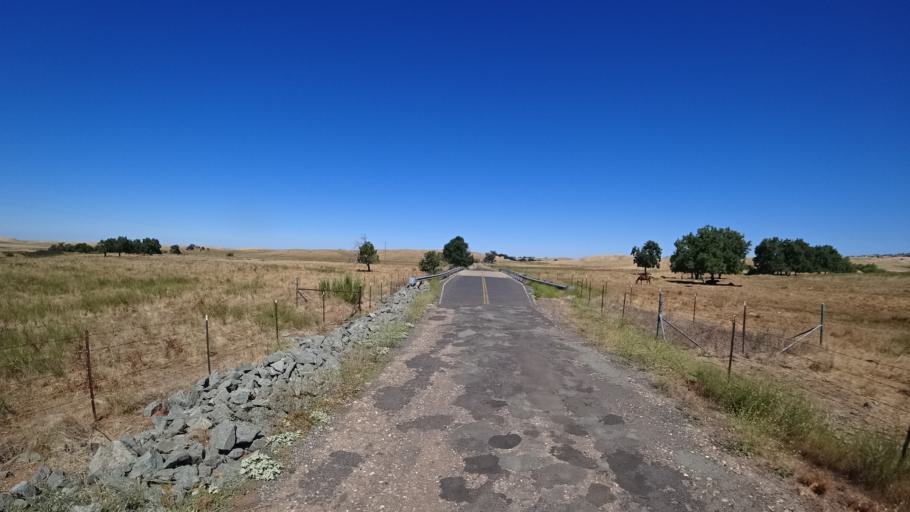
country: US
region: California
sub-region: Calaveras County
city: Rancho Calaveras
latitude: 38.0156
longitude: -120.8271
